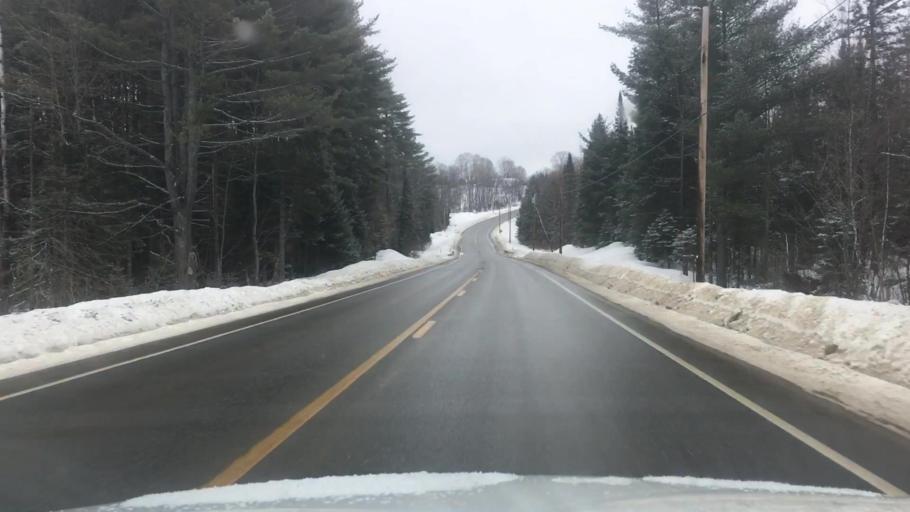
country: US
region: Maine
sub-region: Franklin County
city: Wilton
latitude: 44.5829
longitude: -70.1950
